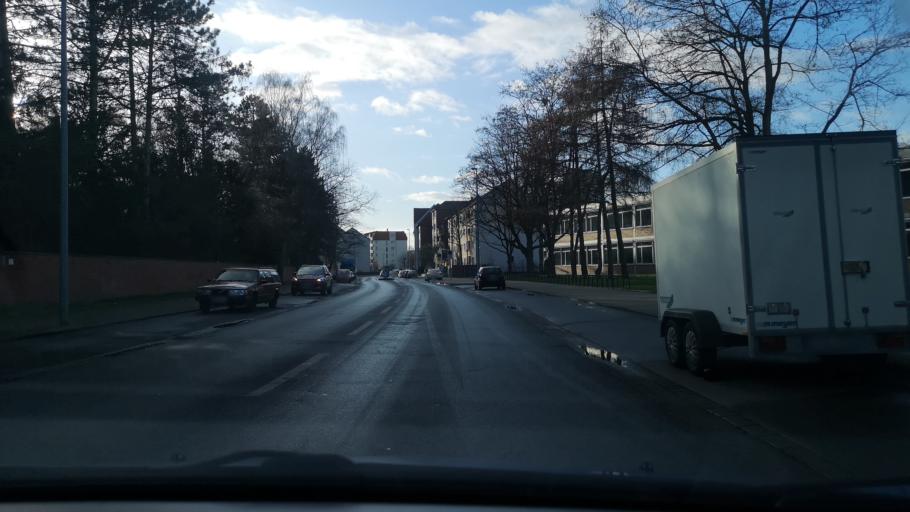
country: DE
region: Lower Saxony
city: Hannover
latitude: 52.4085
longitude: 9.6736
